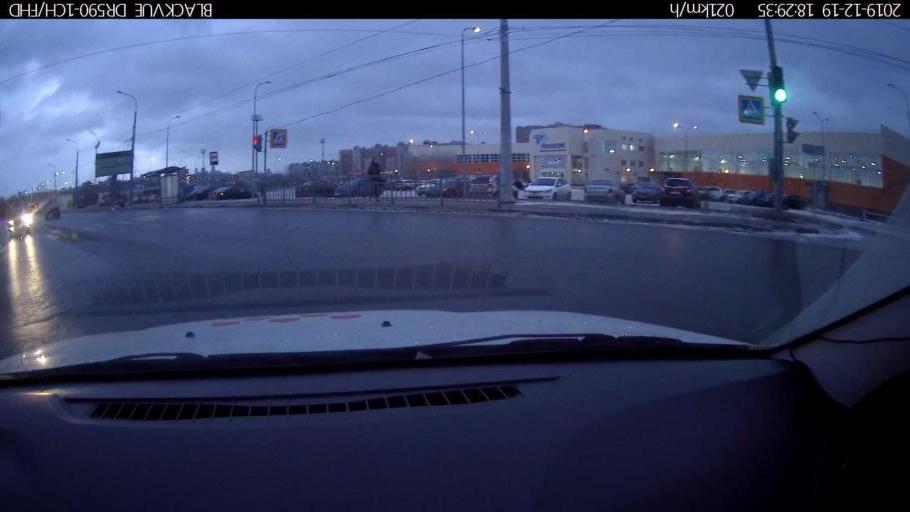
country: RU
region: Nizjnij Novgorod
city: Nizhniy Novgorod
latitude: 56.3399
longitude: 43.9419
